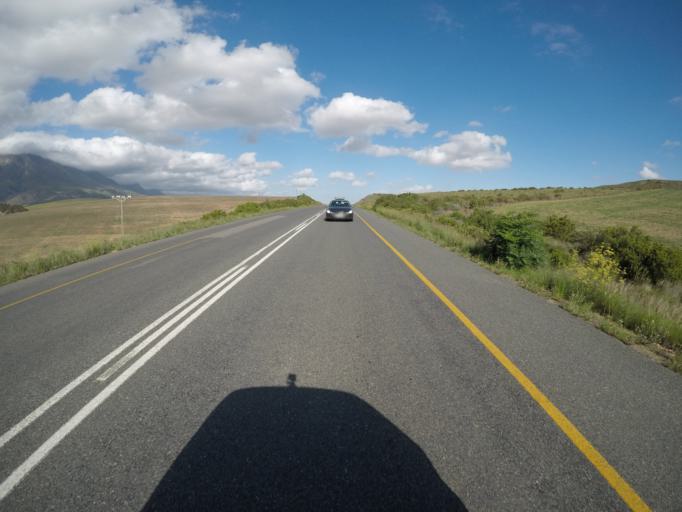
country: ZA
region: Western Cape
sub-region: Overberg District Municipality
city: Swellendam
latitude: -33.9698
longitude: 20.2519
